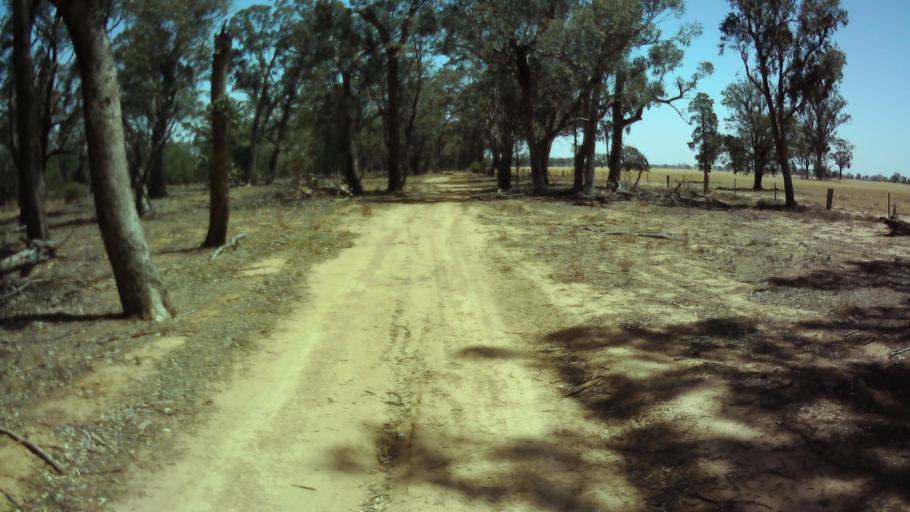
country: AU
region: New South Wales
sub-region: Weddin
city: Grenfell
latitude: -34.0625
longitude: 147.8070
